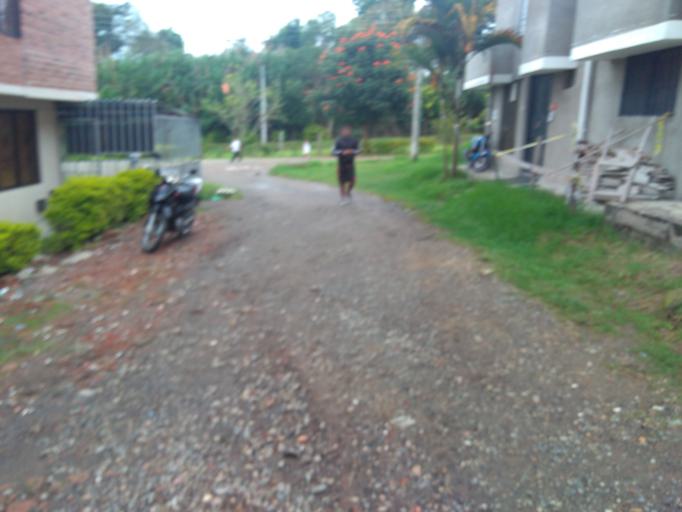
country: CO
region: Cauca
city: Popayan
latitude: 2.4508
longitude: -76.5928
